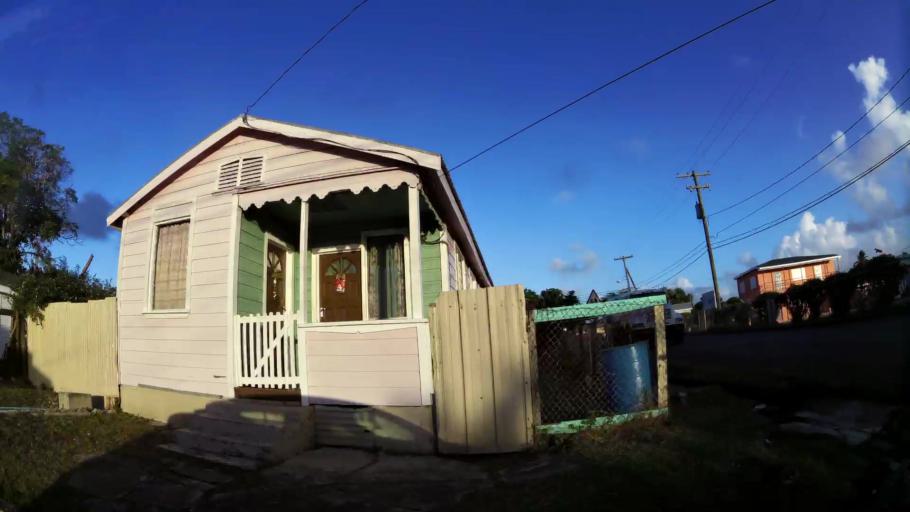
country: AG
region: Saint John
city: Saint John's
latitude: 17.1292
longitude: -61.8486
